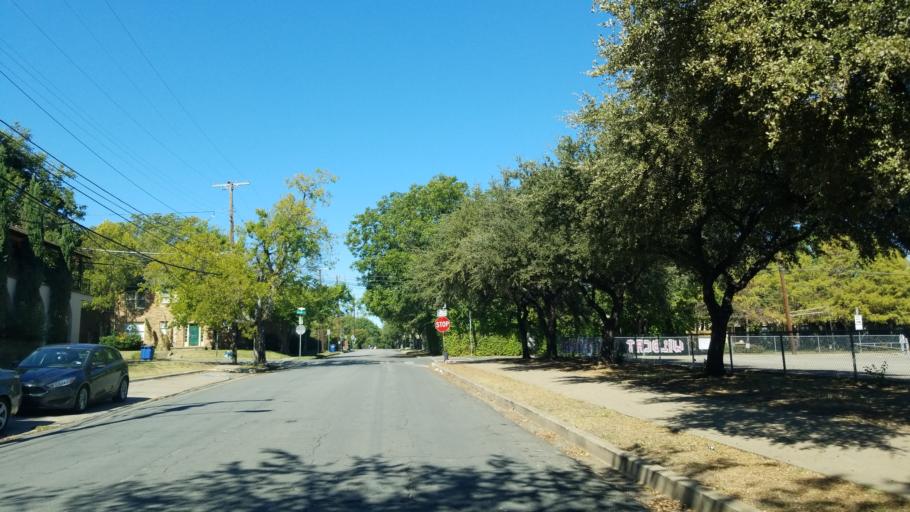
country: US
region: Texas
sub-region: Dallas County
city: Highland Park
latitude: 32.8062
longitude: -96.7521
